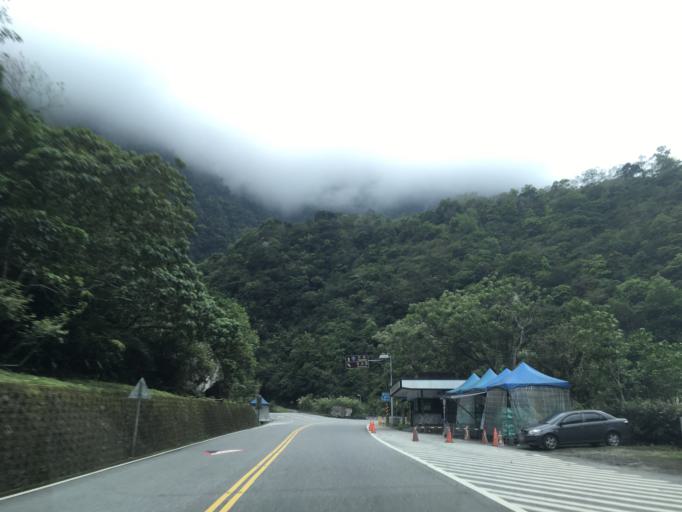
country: TW
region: Taiwan
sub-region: Hualien
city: Hualian
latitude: 24.1726
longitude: 121.5775
